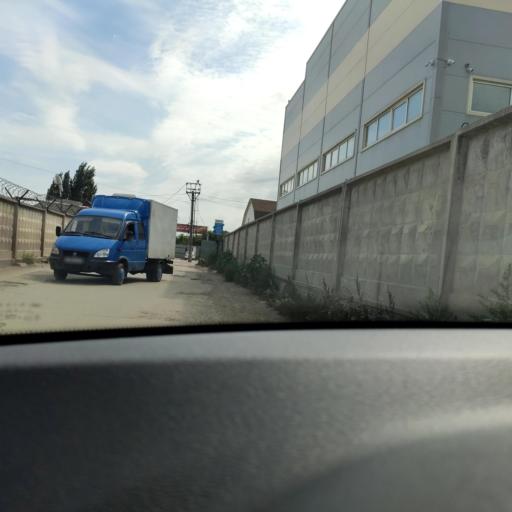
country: RU
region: Samara
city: Samara
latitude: 53.1884
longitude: 50.2382
